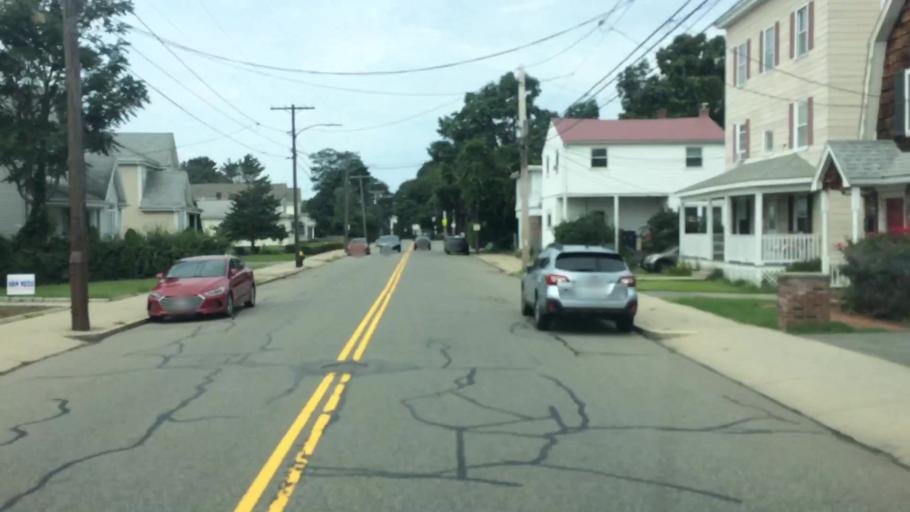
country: US
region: Massachusetts
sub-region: Norfolk County
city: Dedham
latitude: 42.2432
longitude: -71.1410
